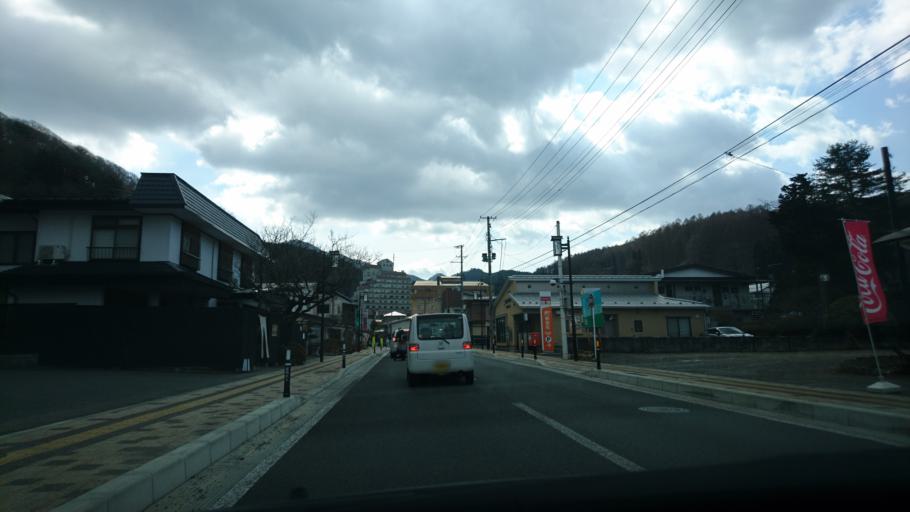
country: JP
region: Iwate
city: Shizukuishi
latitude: 39.6757
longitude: 141.0200
